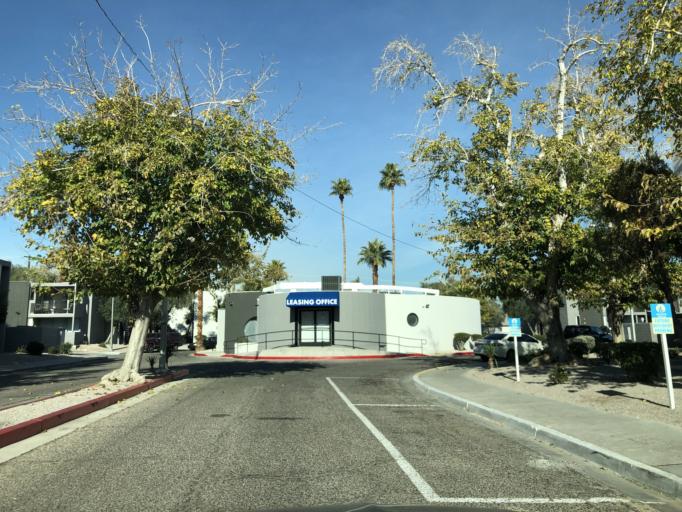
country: US
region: Nevada
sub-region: Clark County
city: Winchester
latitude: 36.1257
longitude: -115.1385
